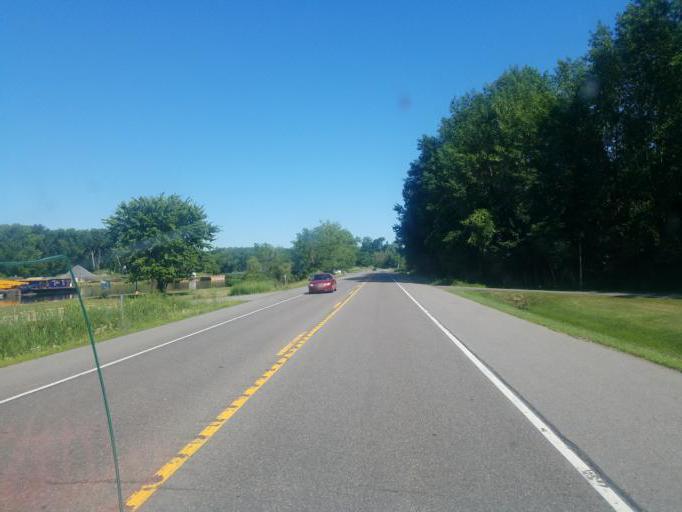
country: US
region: New York
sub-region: Wayne County
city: Lyons
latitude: 43.0616
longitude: -77.0191
